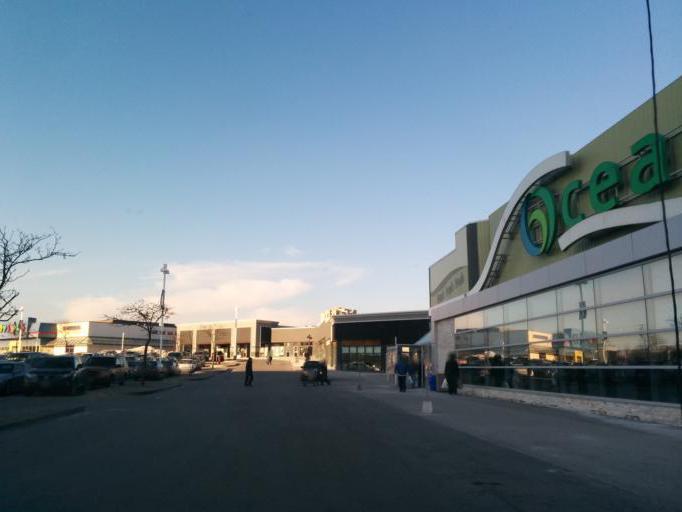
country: CA
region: Ontario
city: Mississauga
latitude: 43.6059
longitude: -79.6493
